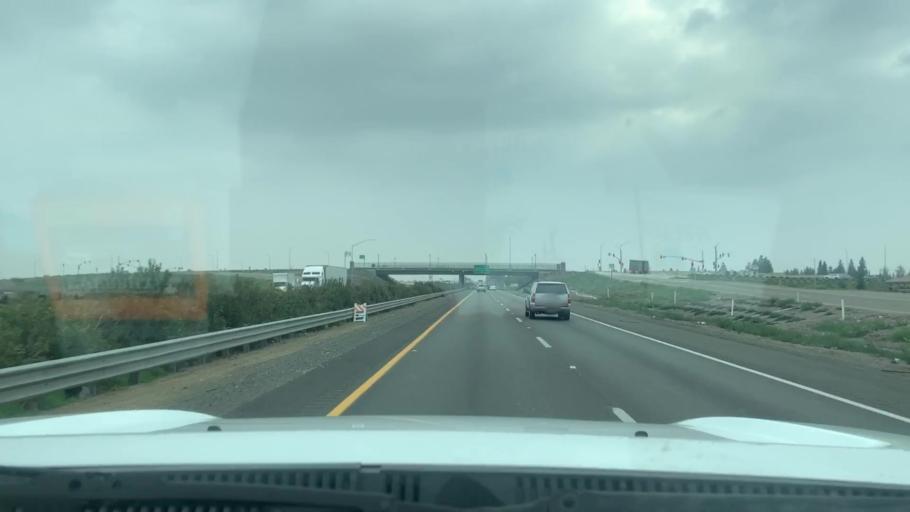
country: US
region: California
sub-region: Tulare County
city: Tulare
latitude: 36.2426
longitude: -119.3475
